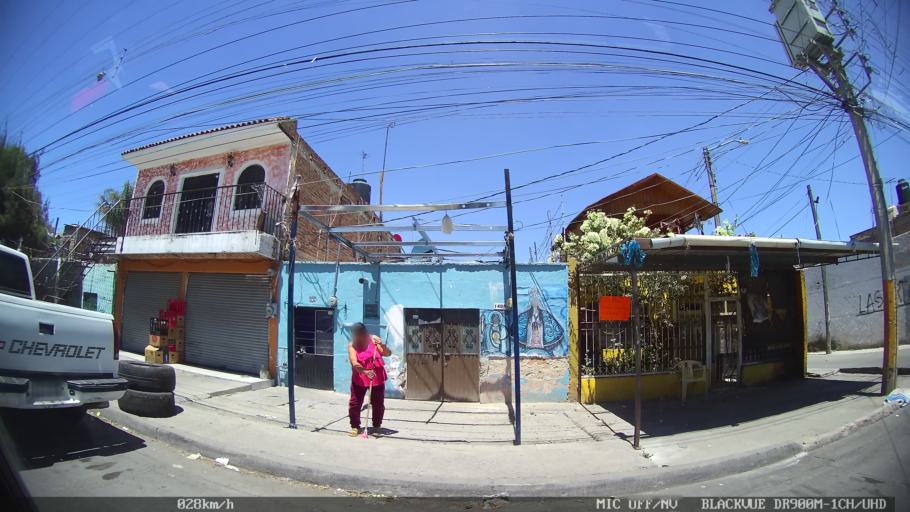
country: MX
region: Jalisco
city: Tlaquepaque
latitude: 20.6559
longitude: -103.2731
